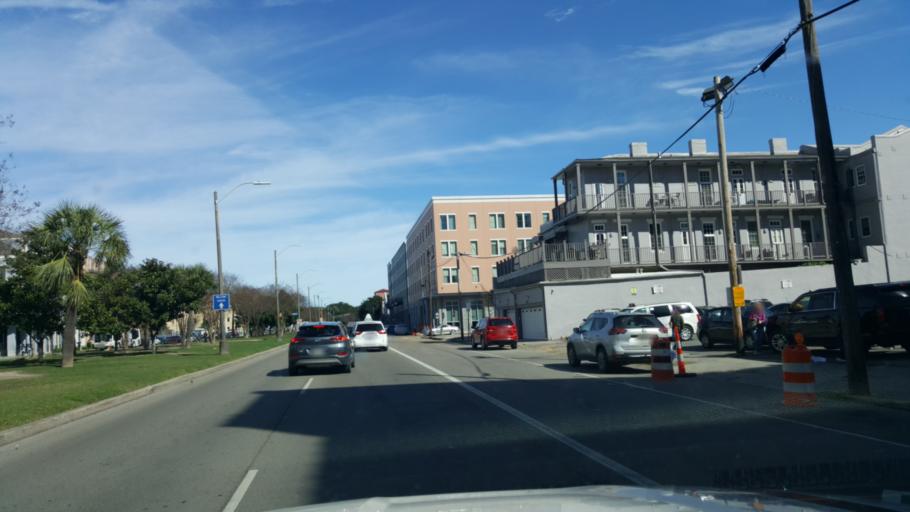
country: US
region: Louisiana
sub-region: Orleans Parish
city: New Orleans
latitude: 29.9573
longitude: -90.0722
